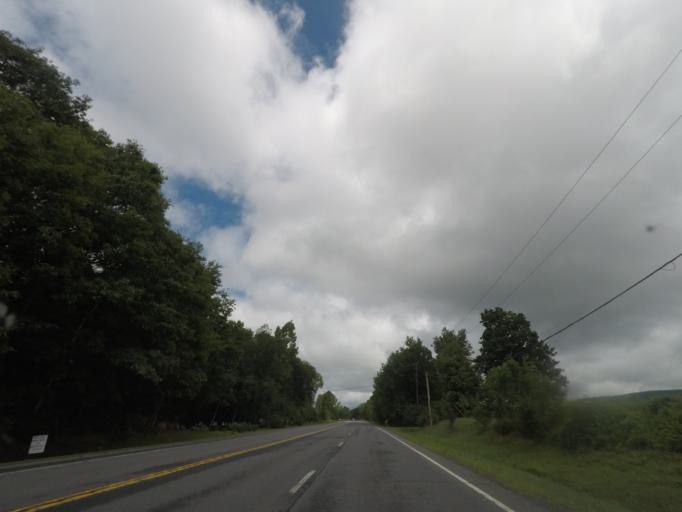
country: US
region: Massachusetts
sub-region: Berkshire County
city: Lanesborough
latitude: 42.5799
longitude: -73.3673
